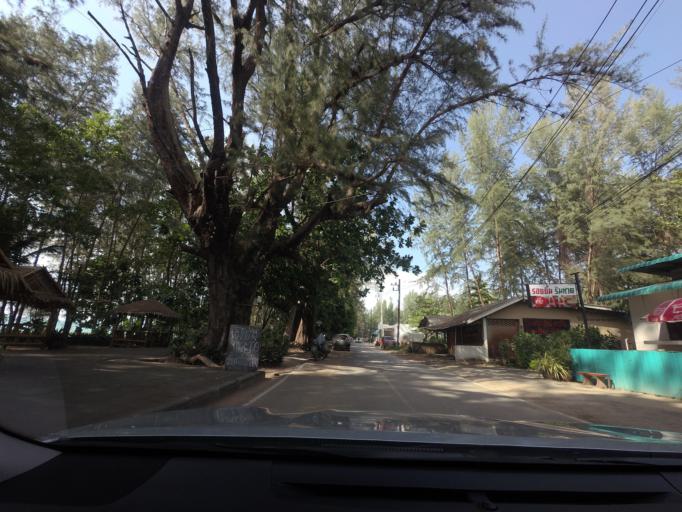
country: TH
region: Phangnga
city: Takua Pa
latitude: 8.7857
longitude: 98.2626
